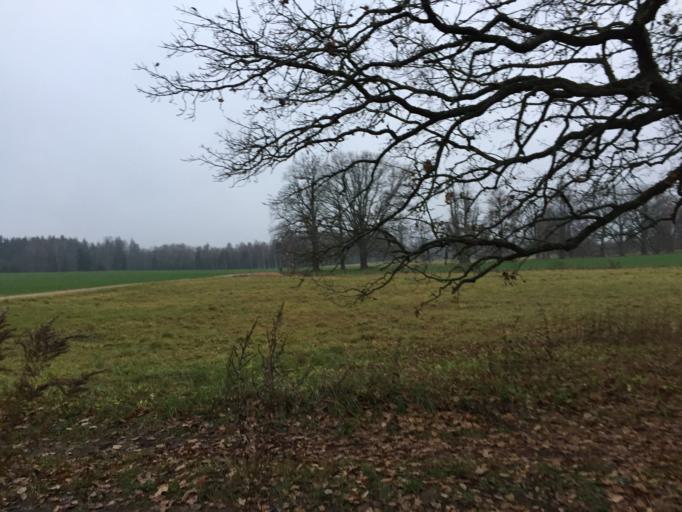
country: LV
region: Koceni
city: Koceni
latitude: 57.5519
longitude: 25.3568
